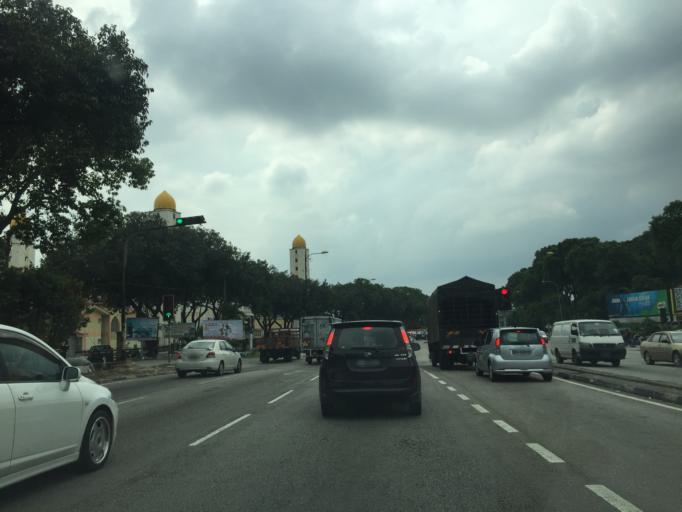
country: MY
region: Selangor
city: Klang
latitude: 3.0239
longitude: 101.4428
